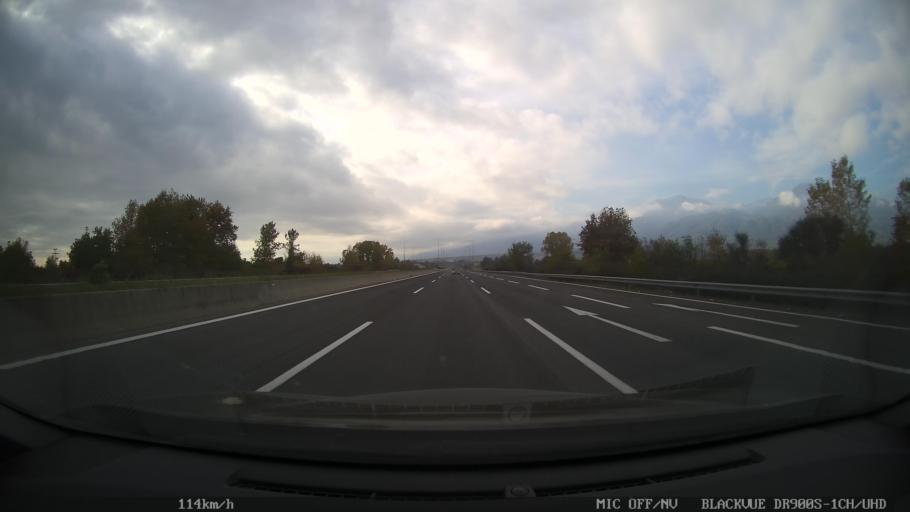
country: GR
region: Central Macedonia
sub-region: Nomos Pierias
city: Dion
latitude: 40.1572
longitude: 22.5433
